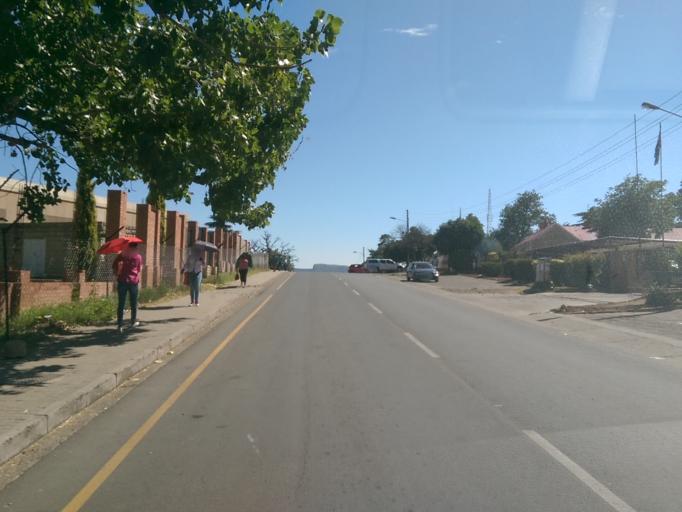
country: LS
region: Maseru
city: Maseru
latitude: -29.3131
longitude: 27.4842
